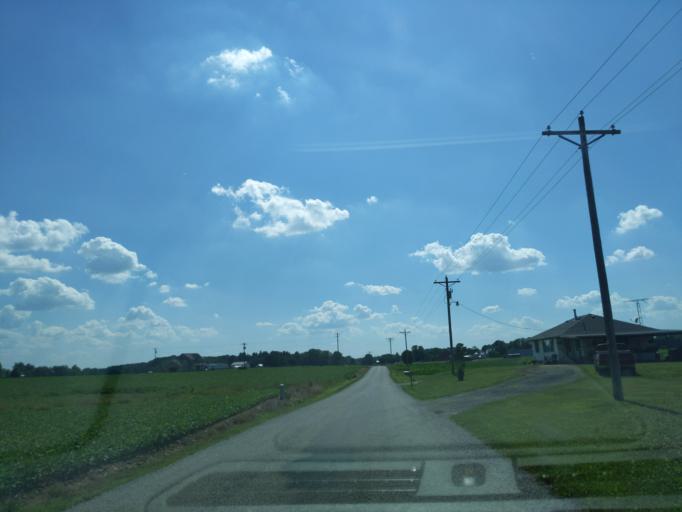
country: US
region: Indiana
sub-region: Ripley County
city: Osgood
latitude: 39.2018
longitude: -85.3685
